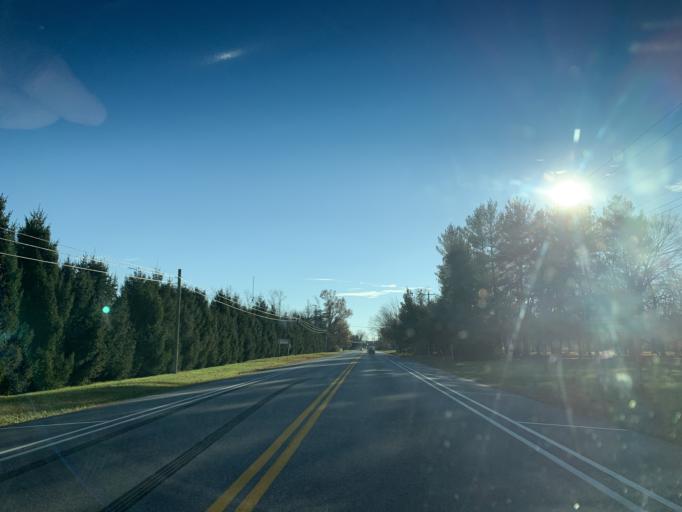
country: US
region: Delaware
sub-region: New Castle County
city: Middletown
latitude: 39.4092
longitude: -75.8651
